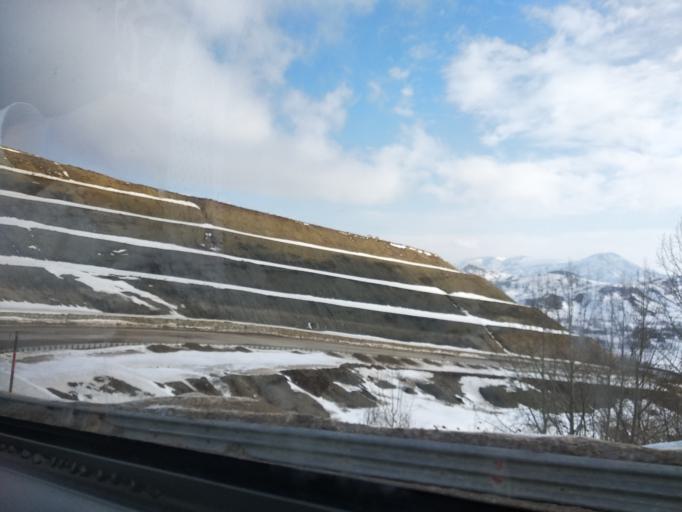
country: TR
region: Erzincan
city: Catalarmut
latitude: 39.8984
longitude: 39.3927
